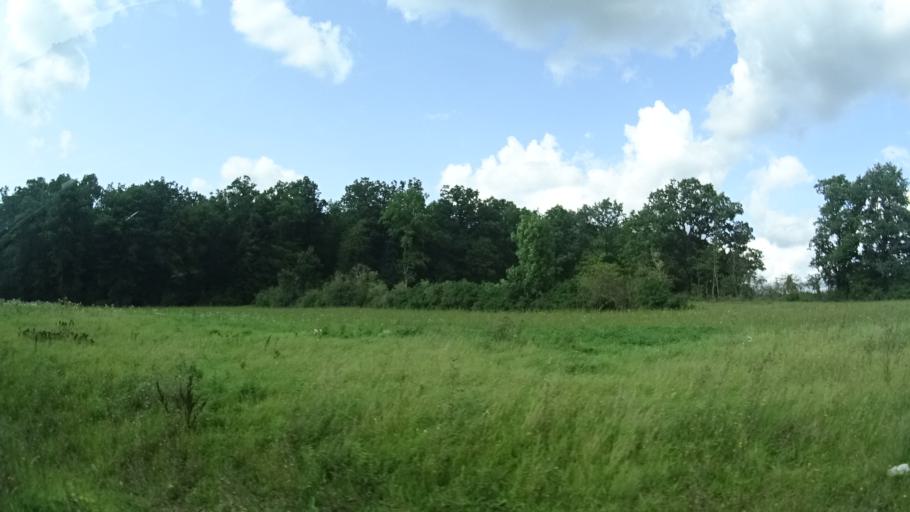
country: DE
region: Bavaria
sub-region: Regierungsbezirk Unterfranken
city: Arnstein
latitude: 49.9234
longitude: 9.9511
